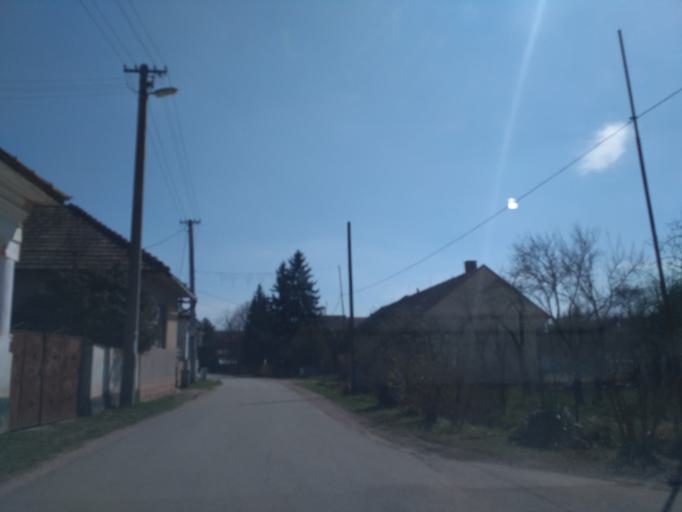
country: SK
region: Kosicky
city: Moldava nad Bodvou
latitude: 48.6534
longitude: 20.9755
